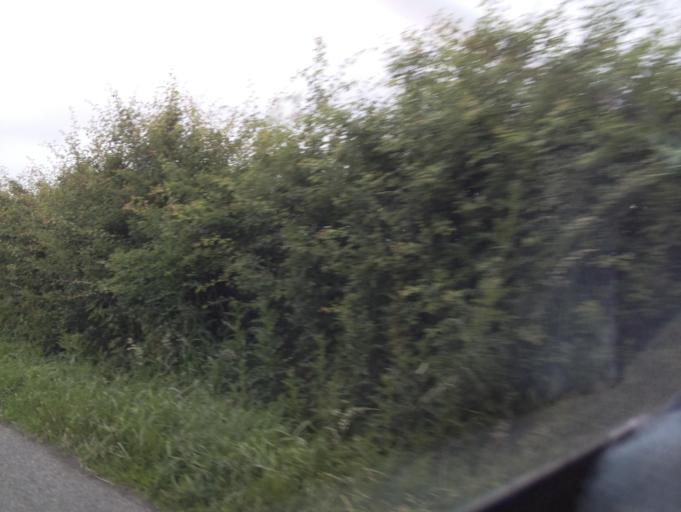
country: GB
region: England
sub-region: Derbyshire
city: Rodsley
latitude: 52.8776
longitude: -1.7401
